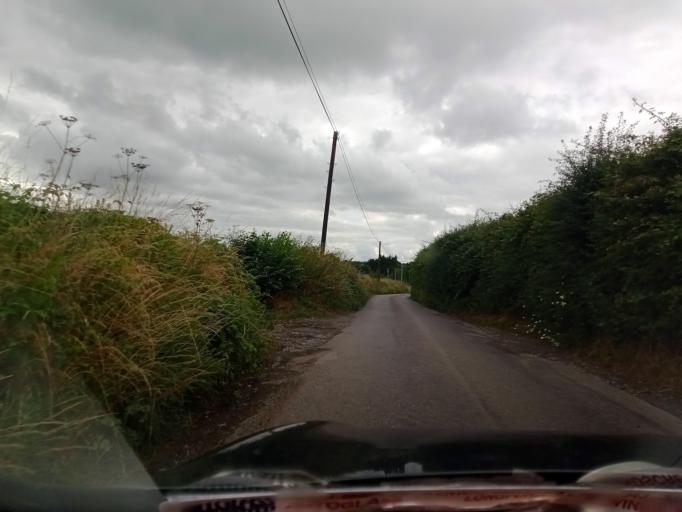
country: IE
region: Leinster
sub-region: Laois
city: Stradbally
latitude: 52.9590
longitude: -7.1945
